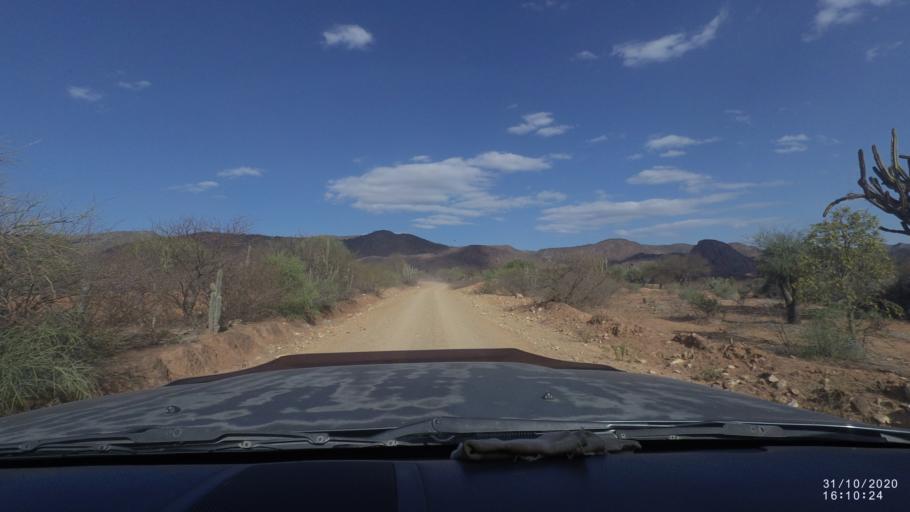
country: BO
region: Chuquisaca
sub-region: Provincia Zudanez
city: Mojocoya
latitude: -18.3829
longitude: -64.6302
